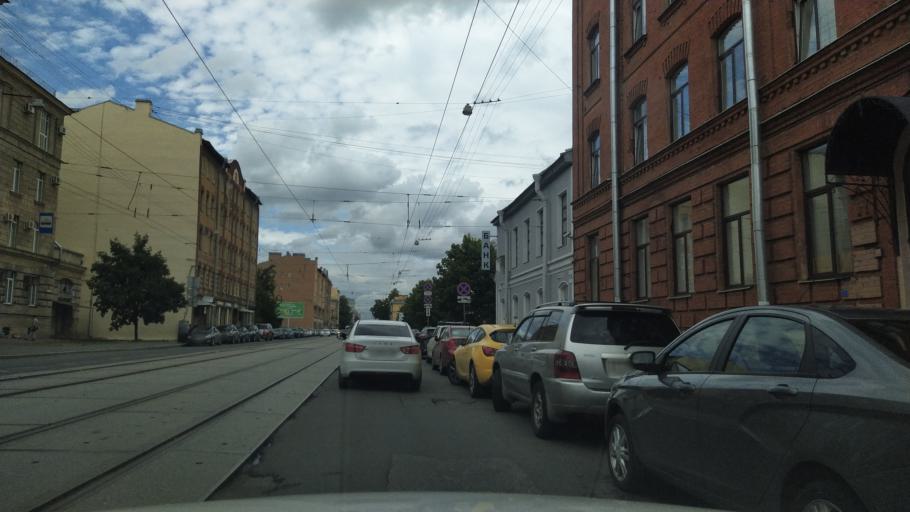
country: RU
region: Leningrad
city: Finlyandskiy
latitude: 59.9641
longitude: 30.3808
